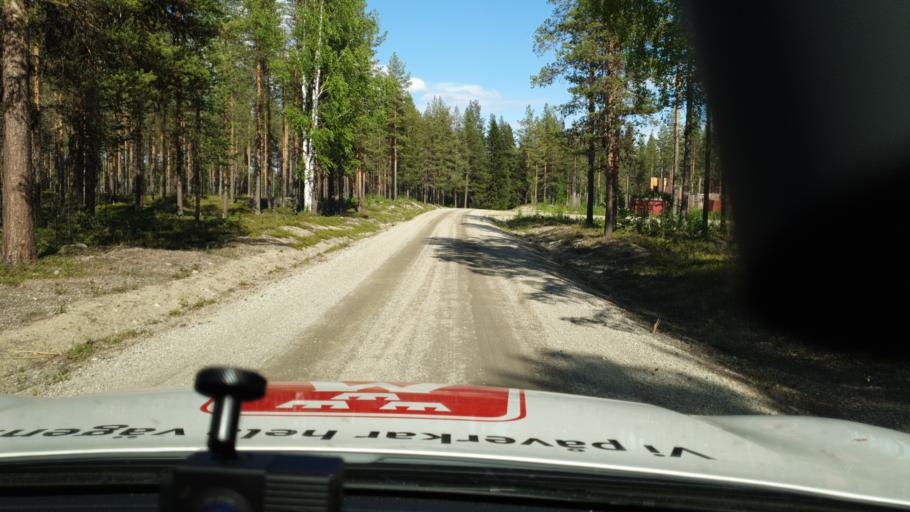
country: SE
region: Vaesterbotten
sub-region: Lycksele Kommun
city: Lycksele
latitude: 64.8957
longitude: 18.5185
